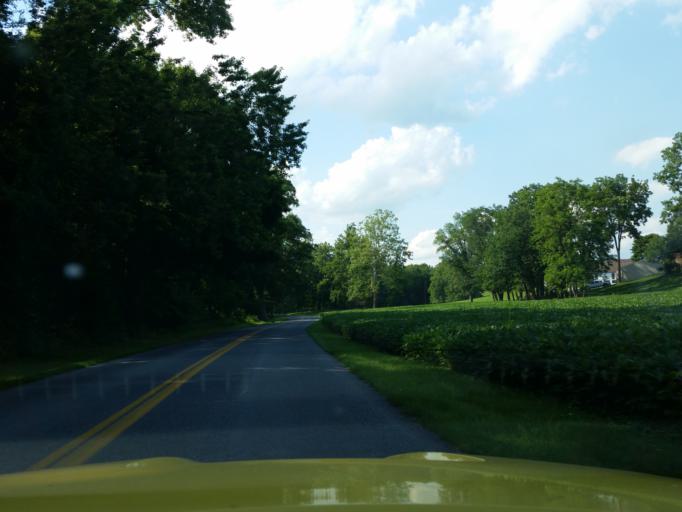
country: US
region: Pennsylvania
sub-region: Lebanon County
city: Annville
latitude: 40.3701
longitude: -76.5346
